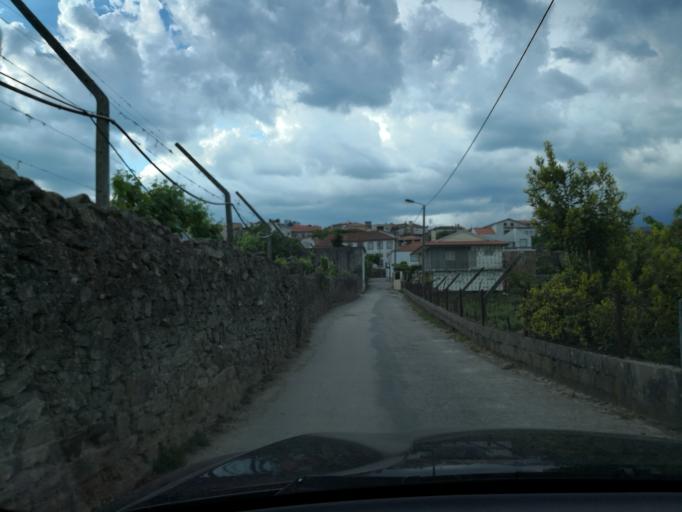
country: PT
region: Vila Real
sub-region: Sabrosa
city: Vilela
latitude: 41.2070
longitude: -7.6595
